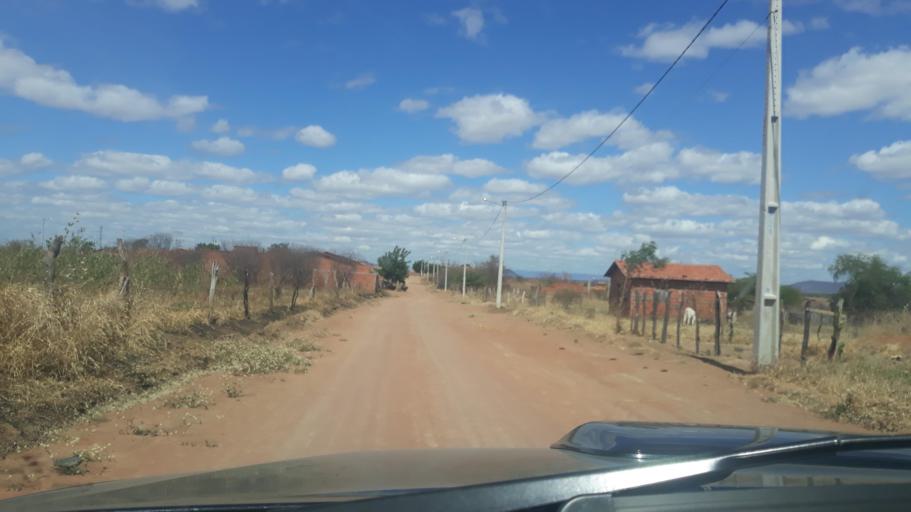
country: BR
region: Bahia
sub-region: Riacho De Santana
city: Riacho de Santana
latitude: -13.9001
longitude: -42.8515
